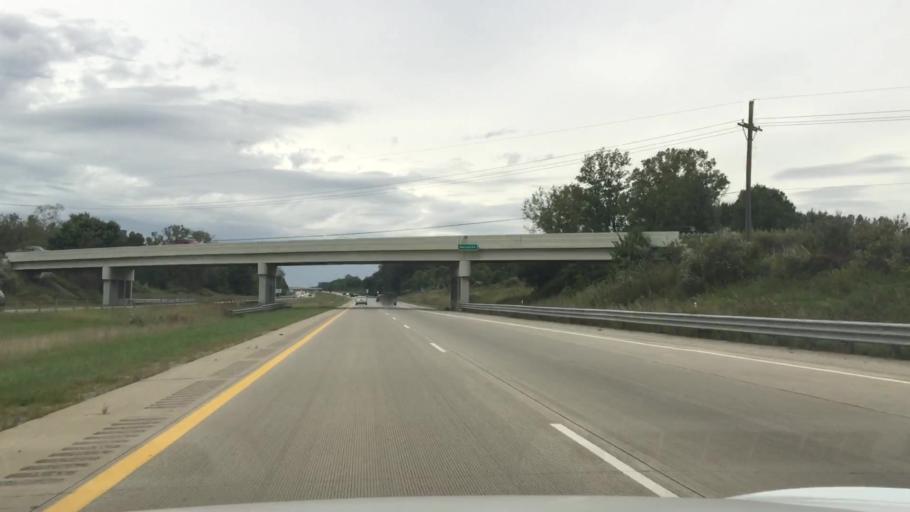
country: US
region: Michigan
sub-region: Macomb County
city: Richmond
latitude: 42.8096
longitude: -82.6339
